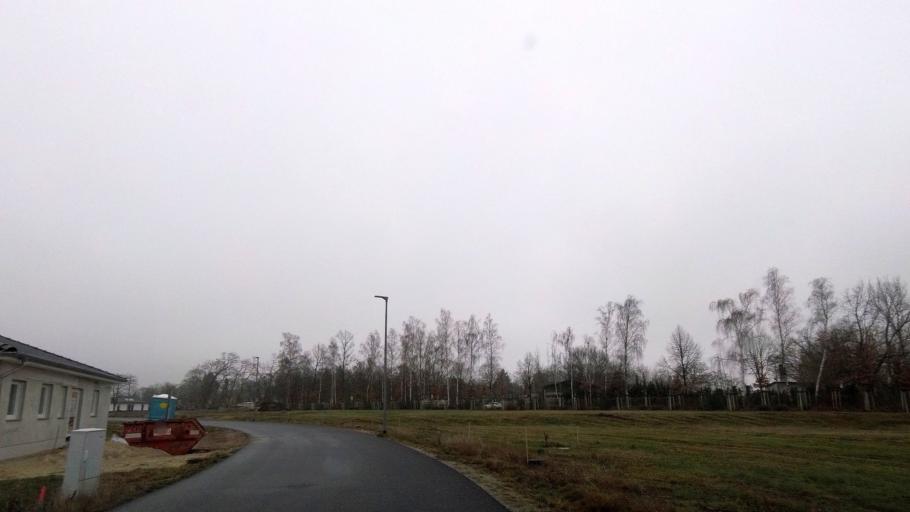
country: DE
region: Brandenburg
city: Juterbog
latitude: 52.0031
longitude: 13.0814
